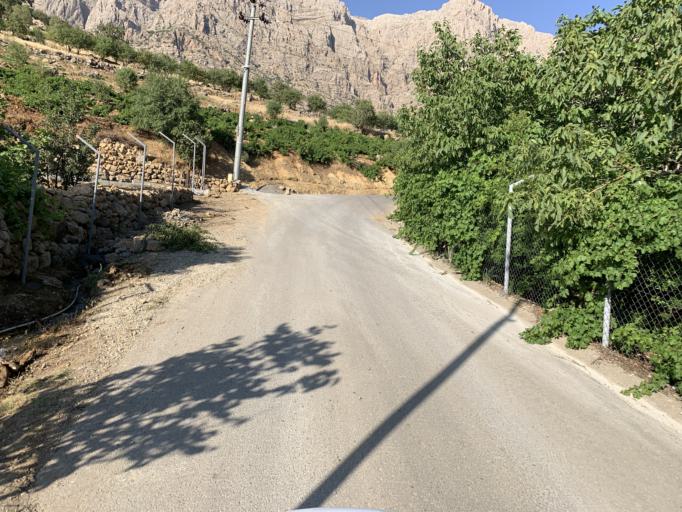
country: IQ
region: As Sulaymaniyah
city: Qeladize
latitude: 35.9917
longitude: 45.1981
